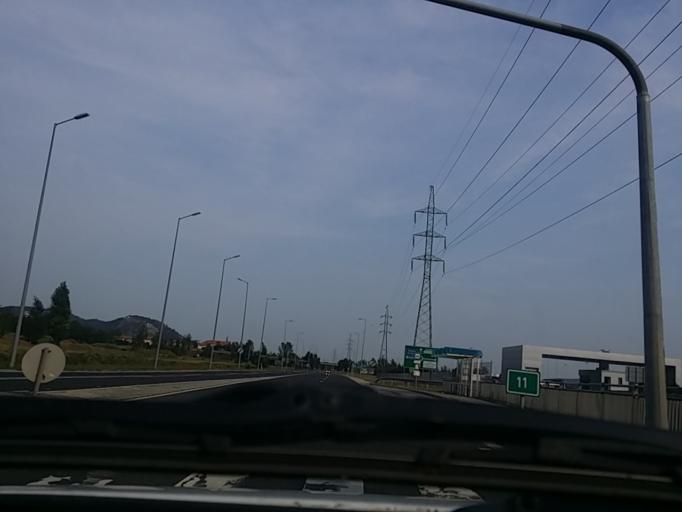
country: HU
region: Pest
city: Toeroekbalint
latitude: 47.4681
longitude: 18.8748
